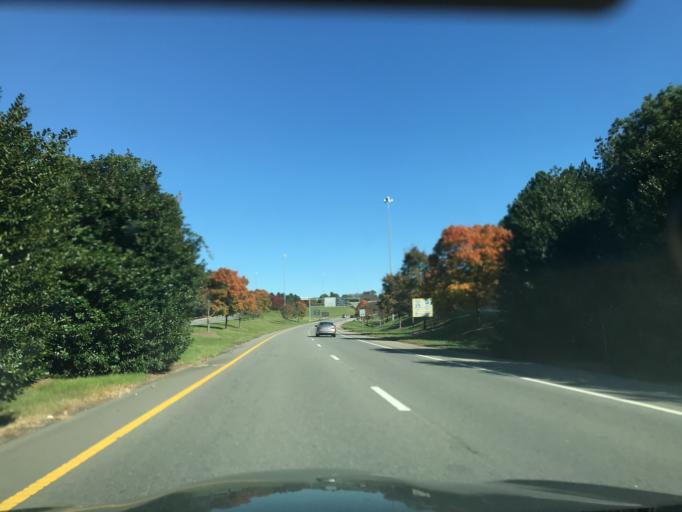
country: US
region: North Carolina
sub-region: Wake County
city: Morrisville
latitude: 35.8630
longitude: -78.8110
